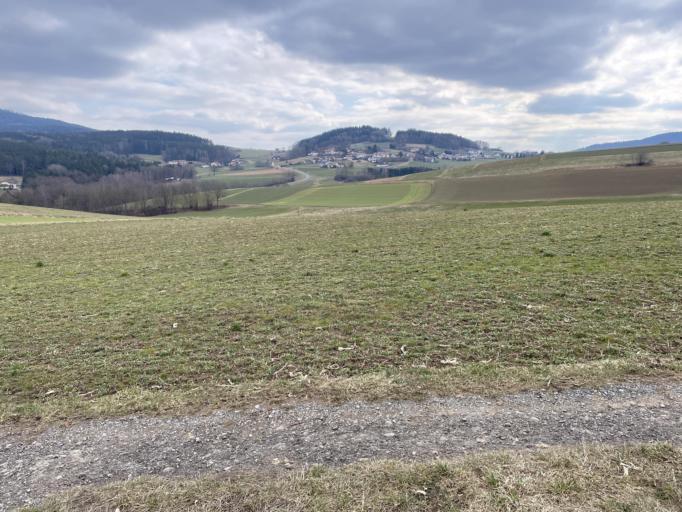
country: DE
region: Bavaria
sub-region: Upper Palatinate
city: Runding
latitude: 49.2278
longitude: 12.7662
